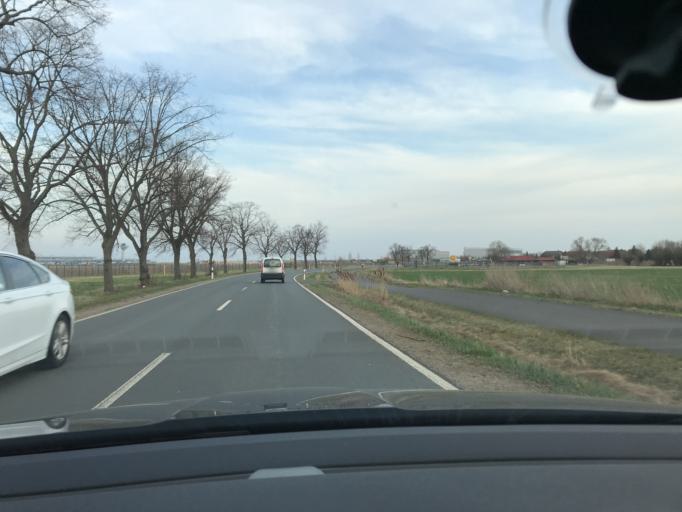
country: DE
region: Brandenburg
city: Schonefeld
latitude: 52.3655
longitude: 13.4691
